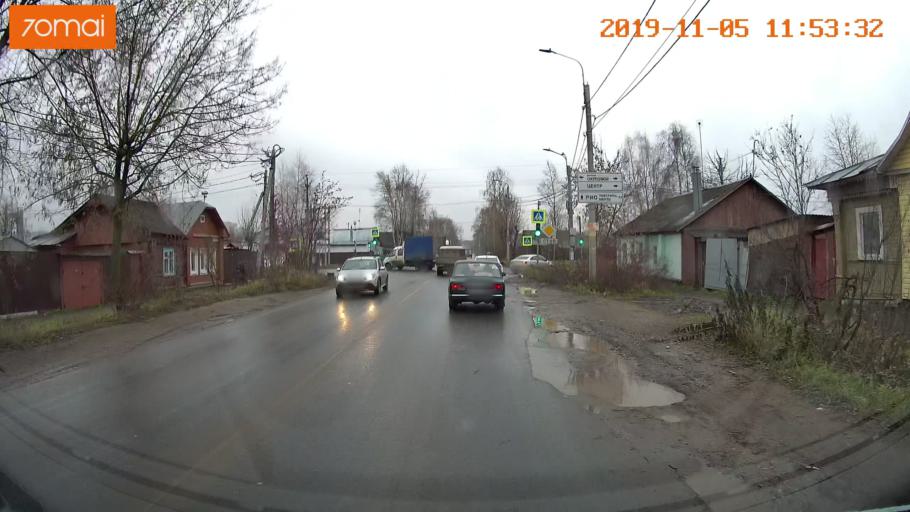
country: RU
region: Ivanovo
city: Bogorodskoye
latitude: 56.9956
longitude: 41.0304
